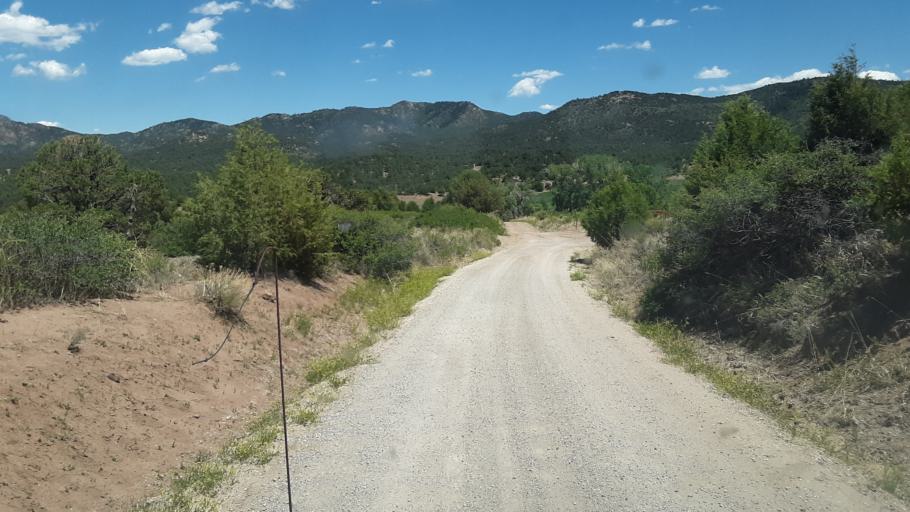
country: US
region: Colorado
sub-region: Custer County
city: Westcliffe
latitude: 38.2836
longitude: -105.6068
